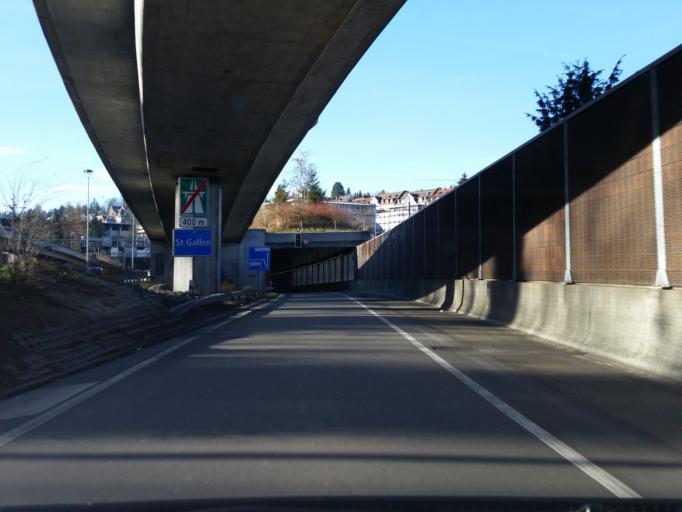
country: CH
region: Saint Gallen
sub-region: Wahlkreis St. Gallen
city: Sankt Gallen
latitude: 47.4337
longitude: 9.3897
